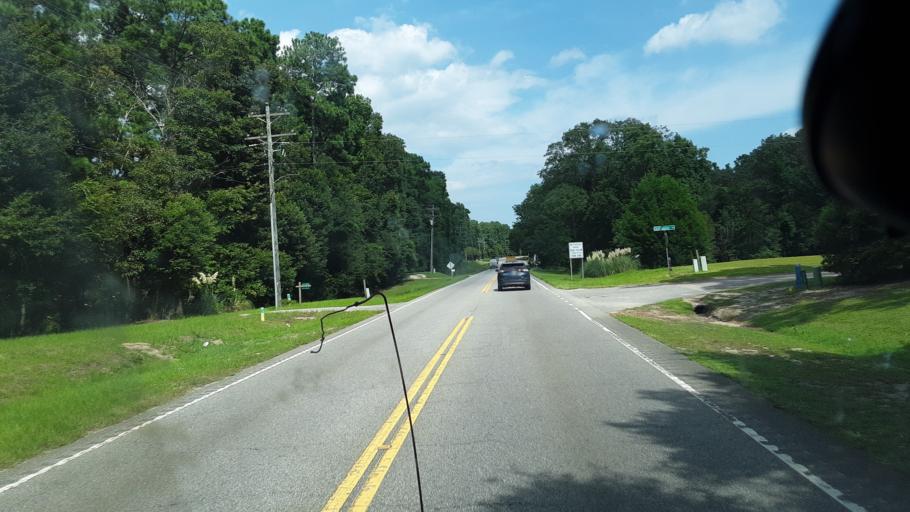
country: US
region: South Carolina
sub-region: Horry County
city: Red Hill
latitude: 33.8213
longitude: -78.9302
